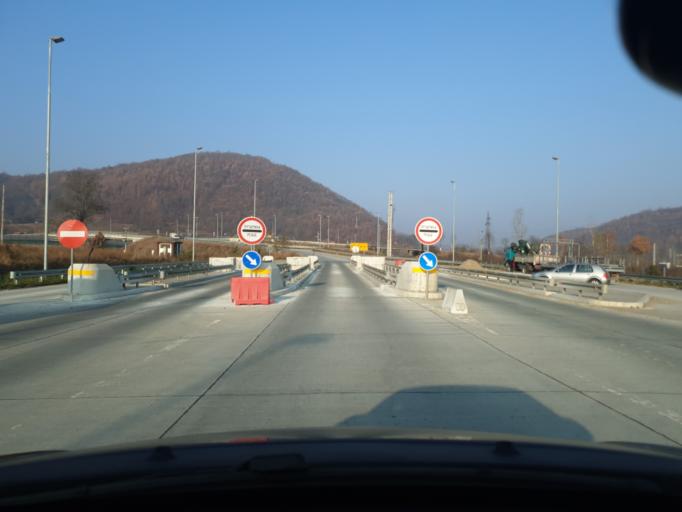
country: RS
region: Central Serbia
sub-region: Jablanicki Okrug
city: Vlasotince
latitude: 42.8860
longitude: 22.0691
